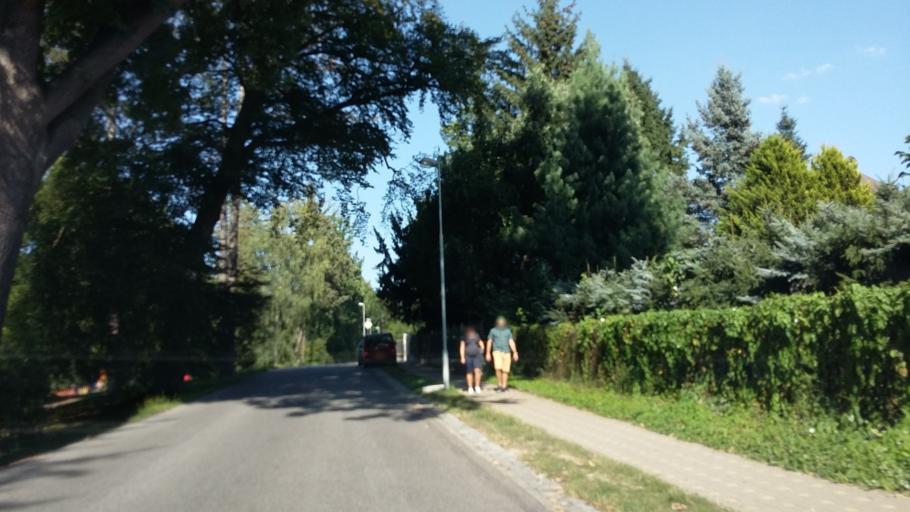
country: CZ
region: Liberecky
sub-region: Okres Semily
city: Turnov
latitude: 50.5968
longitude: 15.1638
